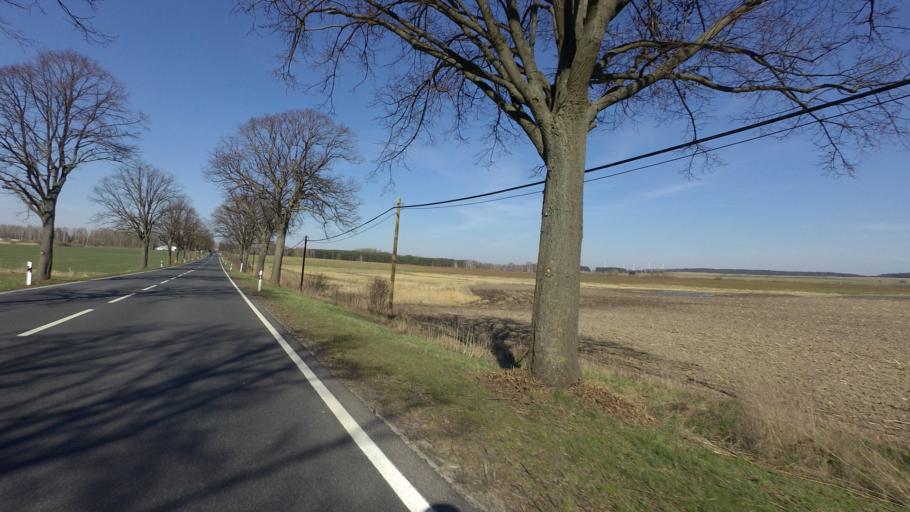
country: DE
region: Brandenburg
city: Angermunde
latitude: 52.9856
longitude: 13.9771
